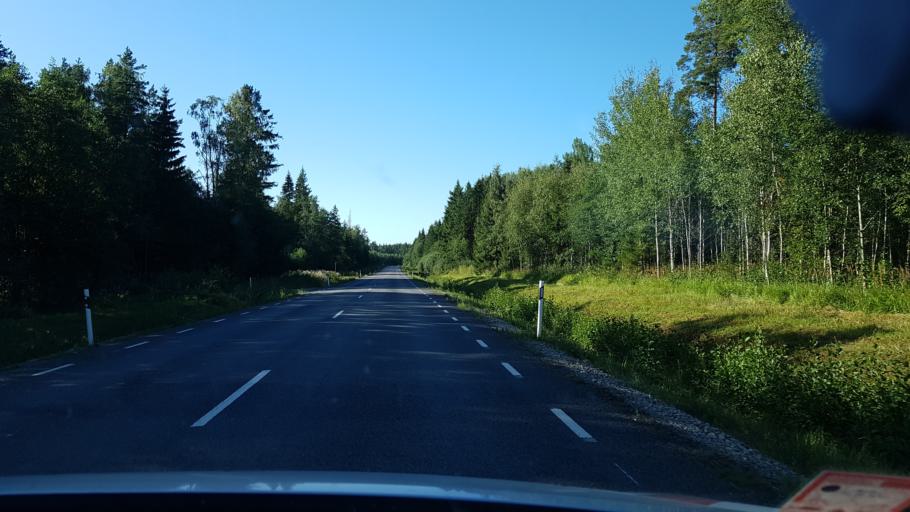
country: EE
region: Jogevamaa
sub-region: Mustvee linn
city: Mustvee
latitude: 59.0571
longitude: 27.0098
